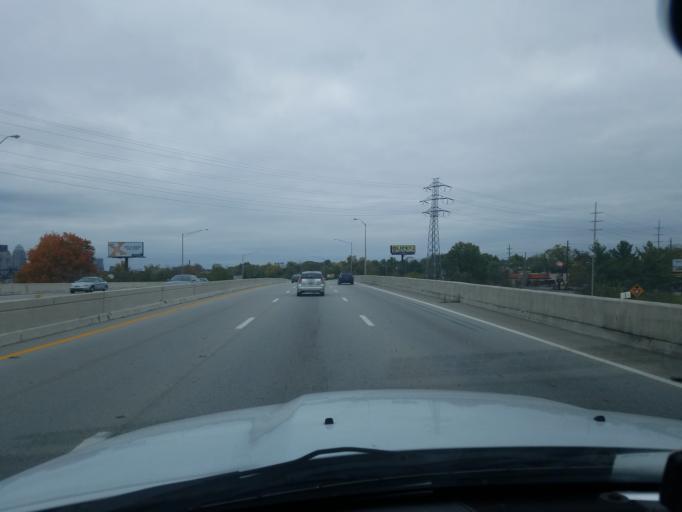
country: US
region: Kentucky
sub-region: Jefferson County
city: Louisville
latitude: 38.2700
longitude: -85.7825
